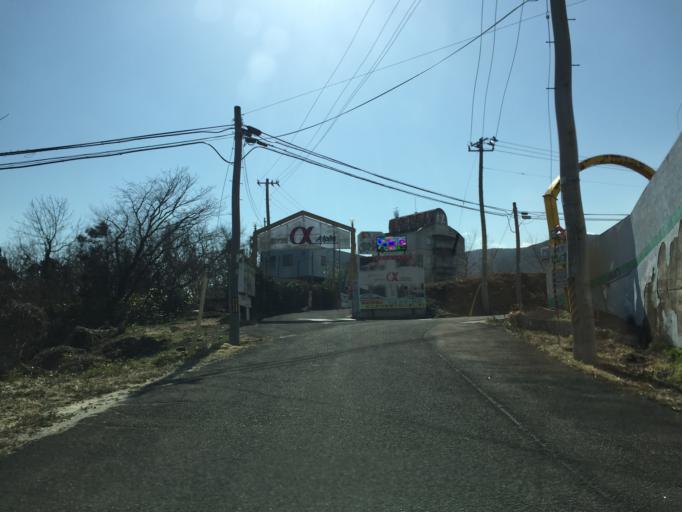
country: JP
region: Fukushima
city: Fukushima-shi
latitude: 37.8250
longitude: 140.4244
